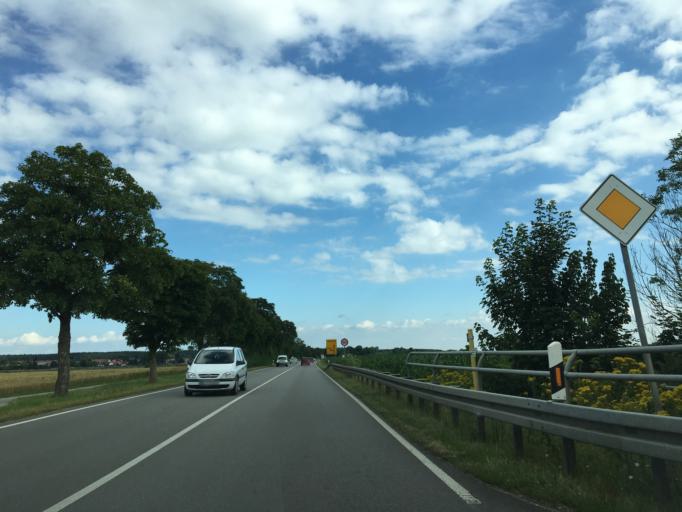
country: DE
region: Bavaria
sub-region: Upper Bavaria
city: Sauerlach
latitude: 47.9385
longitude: 11.6521
